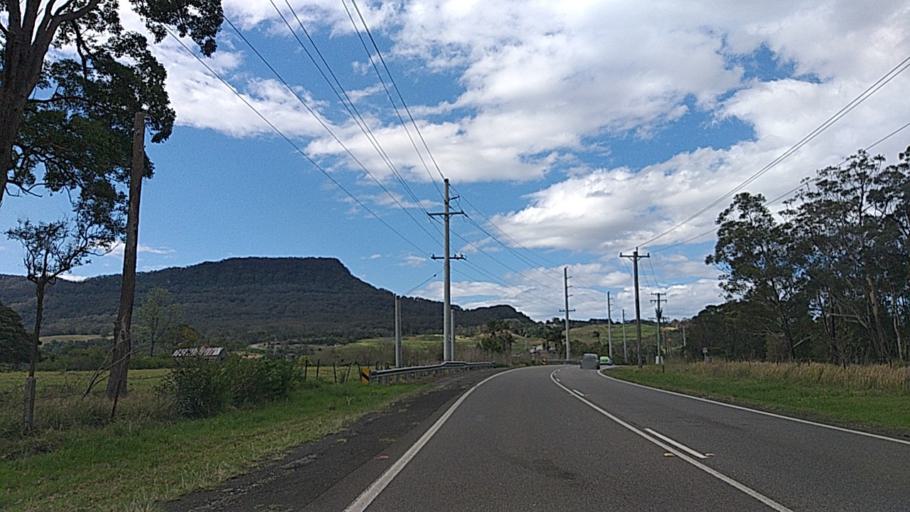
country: AU
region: New South Wales
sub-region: Wollongong
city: Dapto
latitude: -34.4710
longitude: 150.7939
